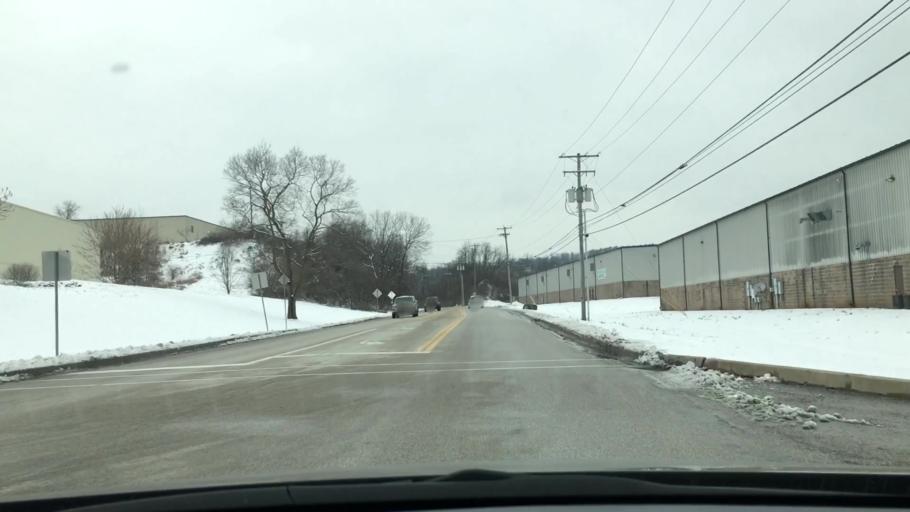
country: US
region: Pennsylvania
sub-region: York County
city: Emigsville
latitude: 40.0128
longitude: -76.7168
